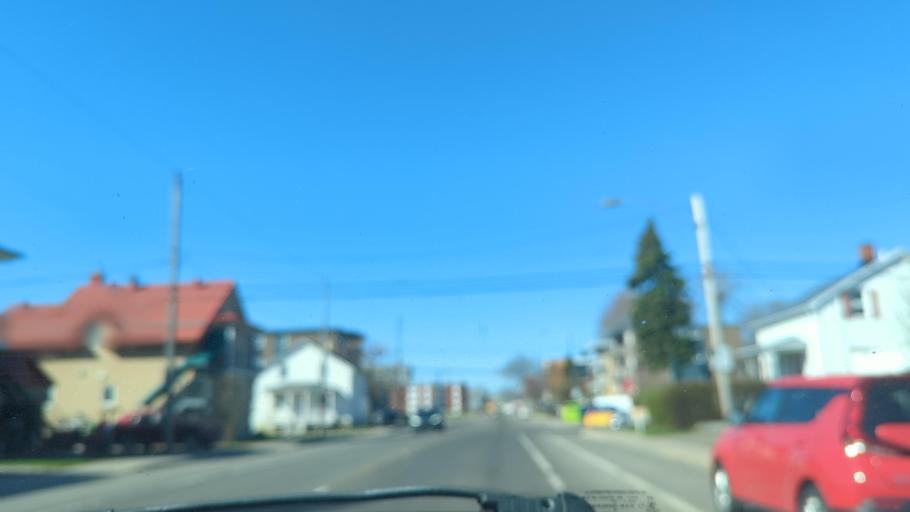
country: CA
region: Quebec
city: Quebec
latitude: 46.8484
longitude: -71.2115
